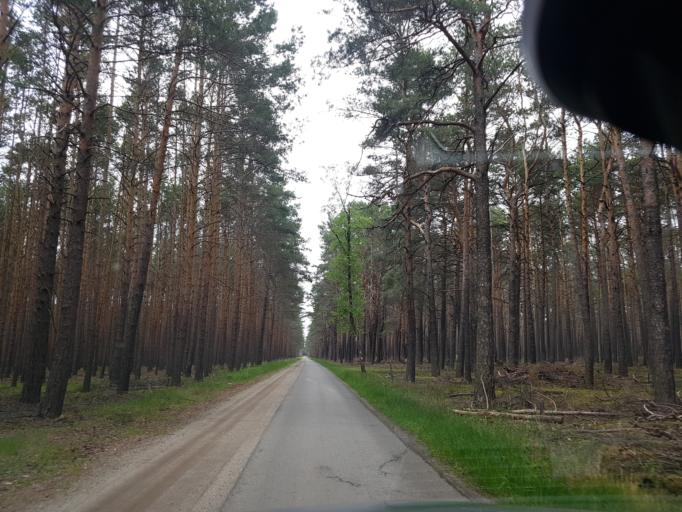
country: DE
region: Brandenburg
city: Crinitz
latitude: 51.6726
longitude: 13.7821
